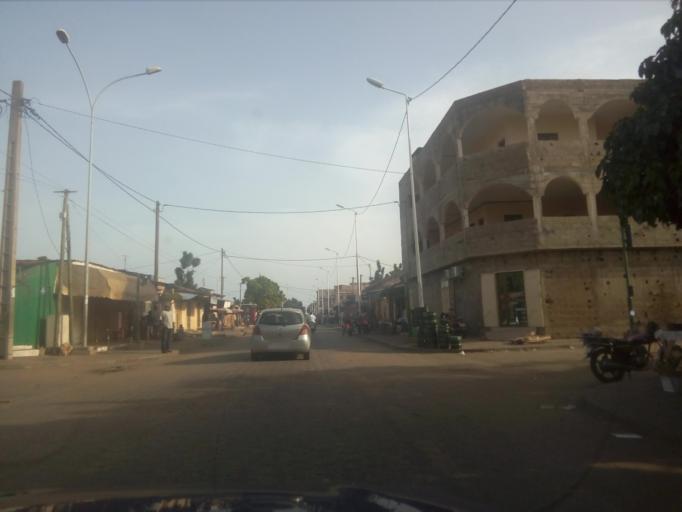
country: TG
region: Maritime
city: Lome
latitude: 6.1422
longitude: 1.2285
